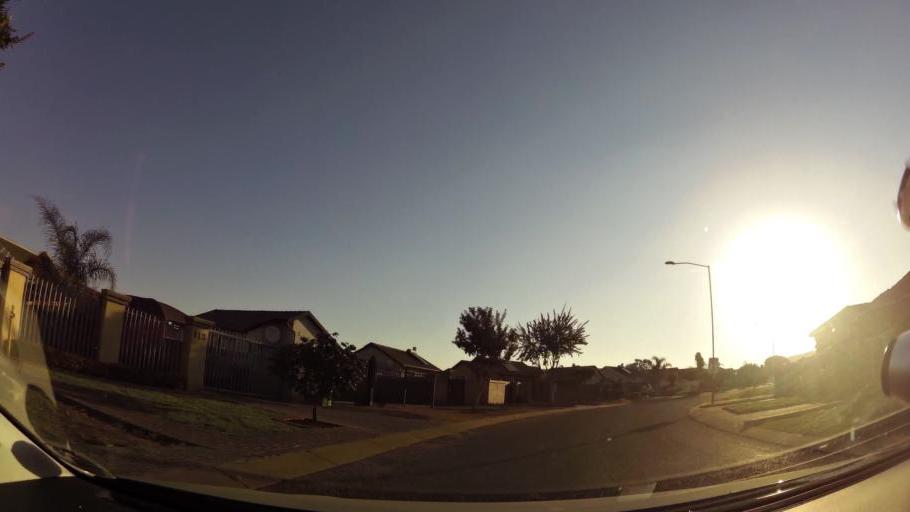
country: ZA
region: Gauteng
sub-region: City of Tshwane Metropolitan Municipality
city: Pretoria
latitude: -25.7430
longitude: 28.1150
